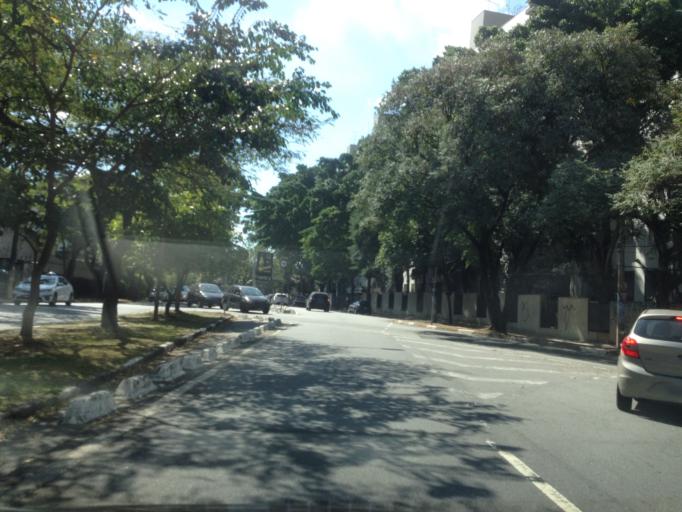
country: BR
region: Sao Paulo
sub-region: Osasco
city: Osasco
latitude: -23.5386
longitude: -46.7195
